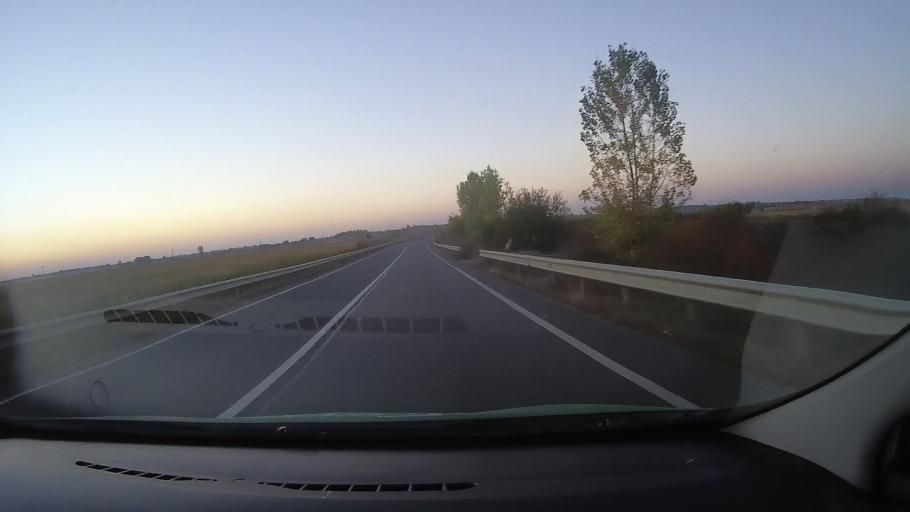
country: RO
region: Bihor
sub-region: Comuna Tarcea
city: Tarcea
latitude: 47.4463
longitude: 22.1870
